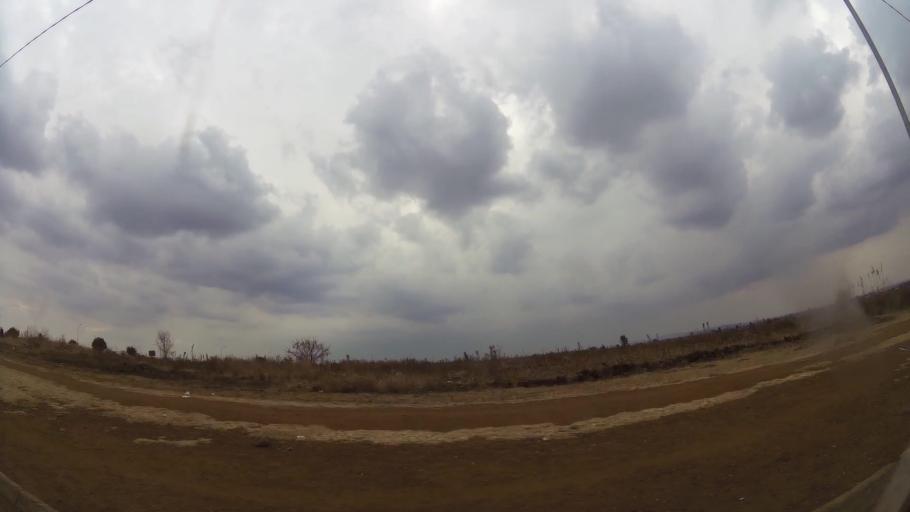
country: ZA
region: Gauteng
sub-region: Ekurhuleni Metropolitan Municipality
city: Germiston
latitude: -26.3833
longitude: 28.1466
